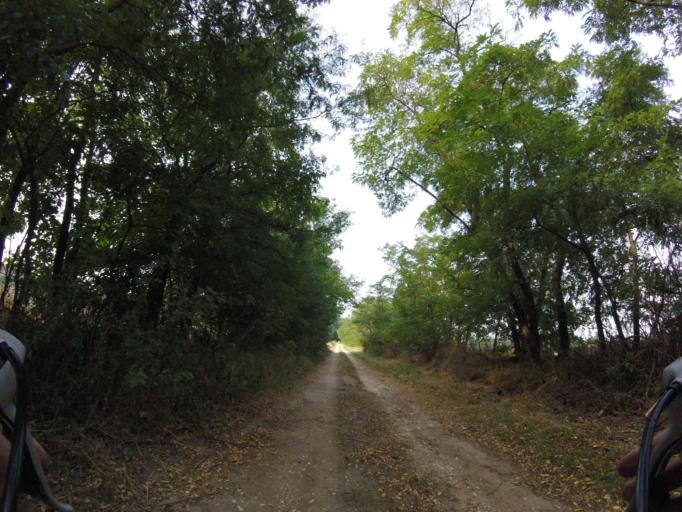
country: HU
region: Veszprem
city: Papa
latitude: 47.2758
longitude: 17.5134
